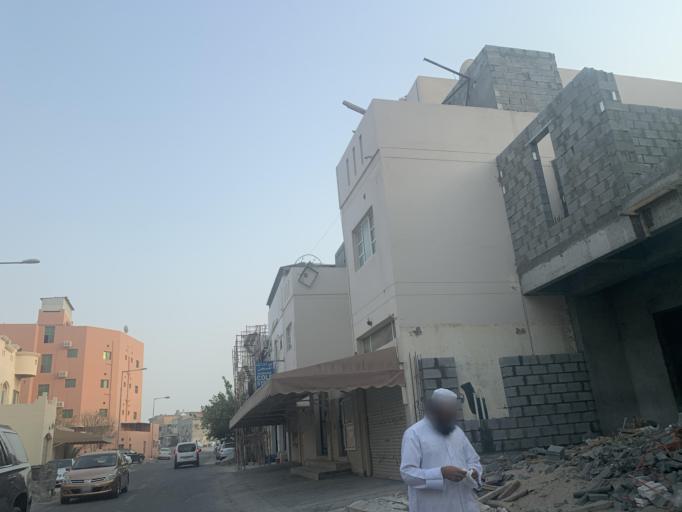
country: BH
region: Manama
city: Jidd Hafs
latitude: 26.2236
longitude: 50.5174
